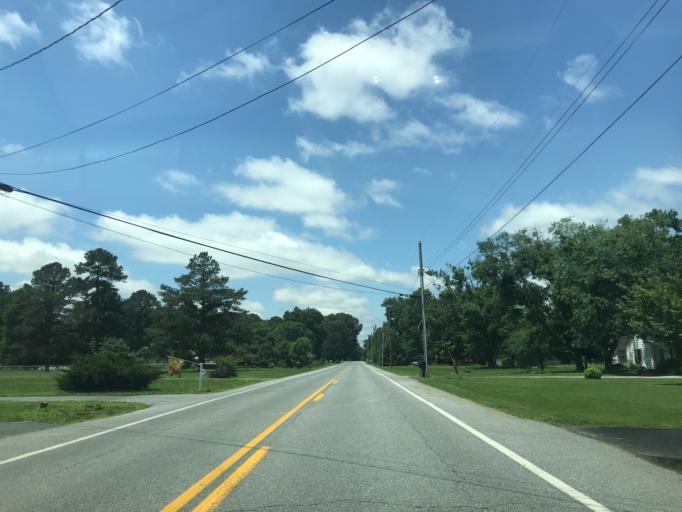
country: US
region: Maryland
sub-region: Caroline County
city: Federalsburg
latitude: 38.6959
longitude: -75.7461
